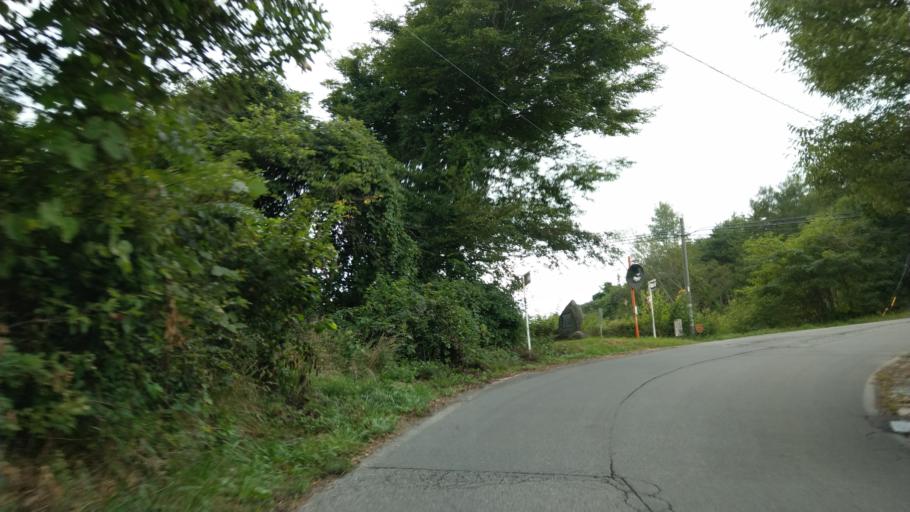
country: JP
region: Nagano
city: Komoro
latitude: 36.3097
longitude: 138.3938
